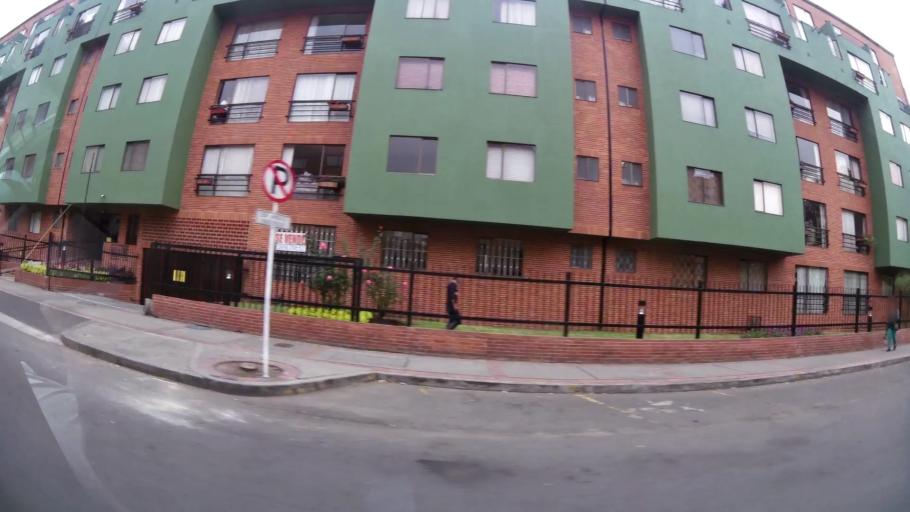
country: CO
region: Bogota D.C.
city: Bogota
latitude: 4.6584
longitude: -74.1090
